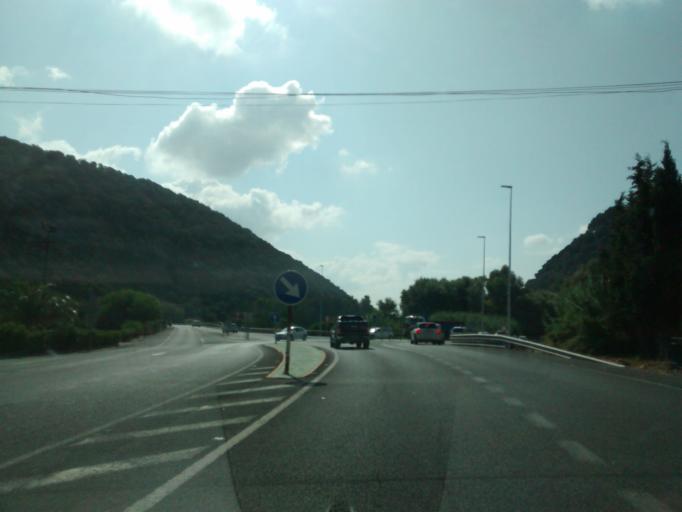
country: ES
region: Andalusia
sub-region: Provincia de Cadiz
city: Vejer de la Frontera
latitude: 36.2596
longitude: -5.9613
